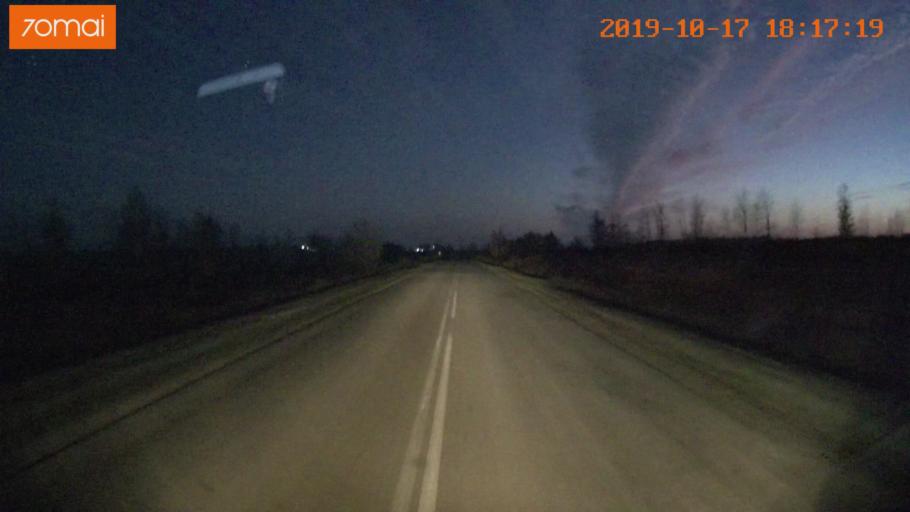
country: RU
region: Tula
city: Kurkino
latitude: 53.3915
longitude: 38.5058
